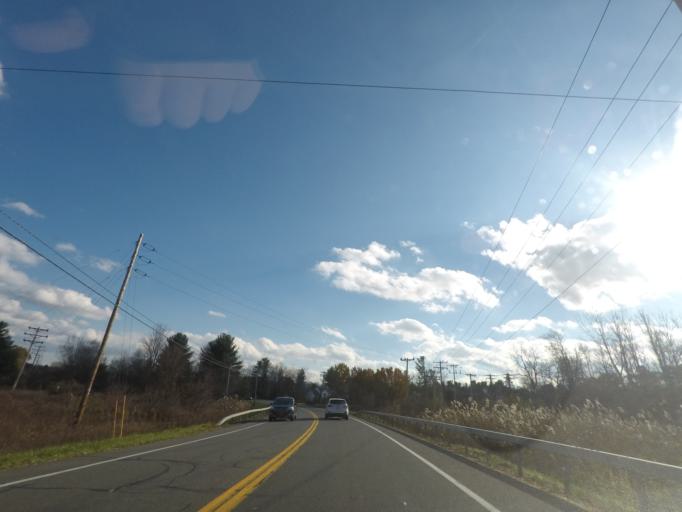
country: US
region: New York
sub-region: Schenectady County
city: Niskayuna
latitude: 42.8063
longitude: -73.8662
